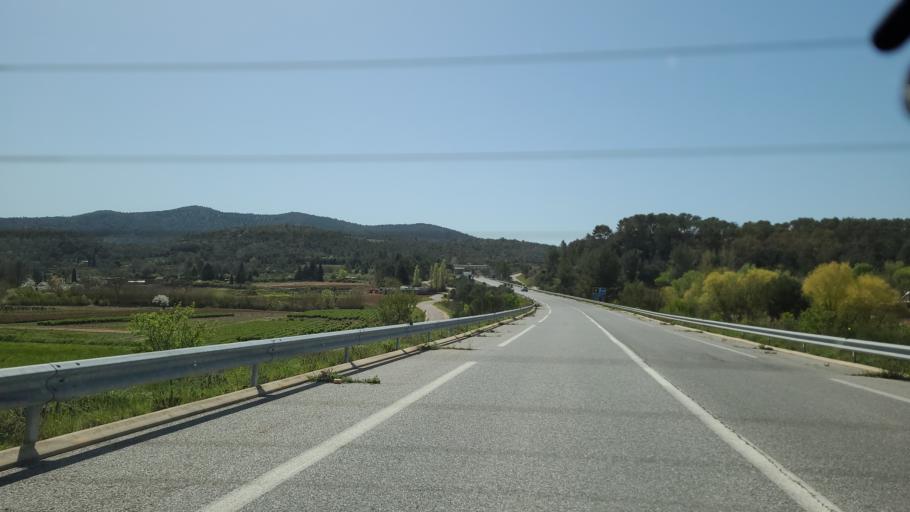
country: FR
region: Provence-Alpes-Cote d'Azur
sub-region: Departement du Var
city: Carnoules
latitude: 43.2974
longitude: 6.2009
